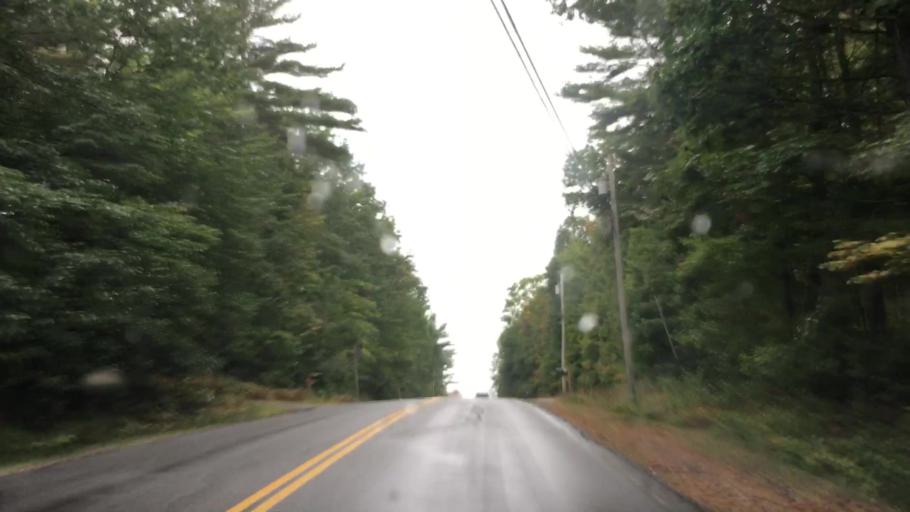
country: US
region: Maine
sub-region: Cumberland County
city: Raymond
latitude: 43.9277
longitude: -70.3752
